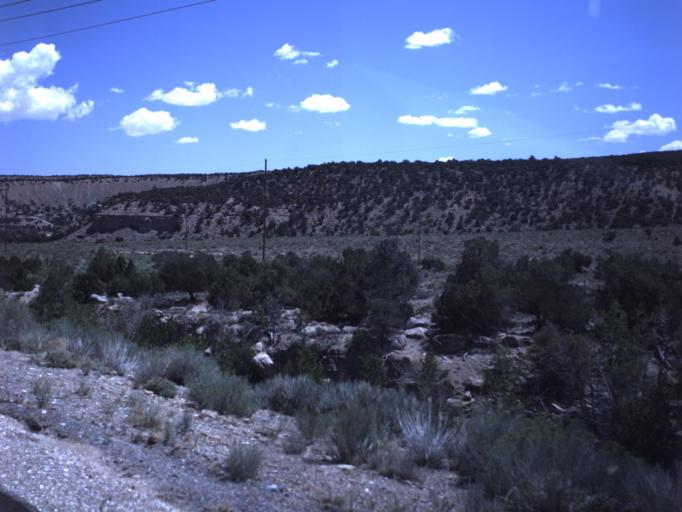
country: US
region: Utah
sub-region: Emery County
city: Orangeville
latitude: 39.2697
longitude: -111.1490
